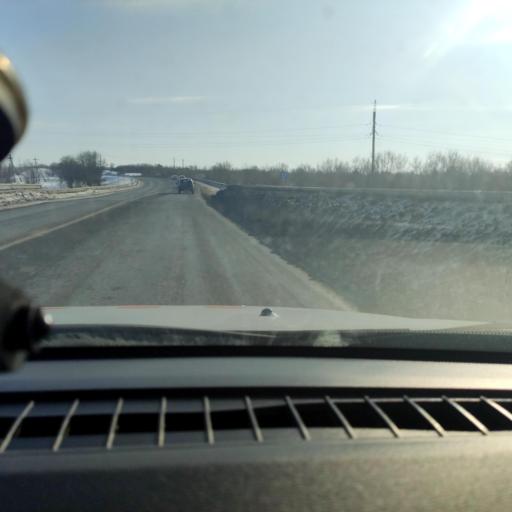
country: RU
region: Samara
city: Smyshlyayevka
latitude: 53.2801
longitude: 50.4621
